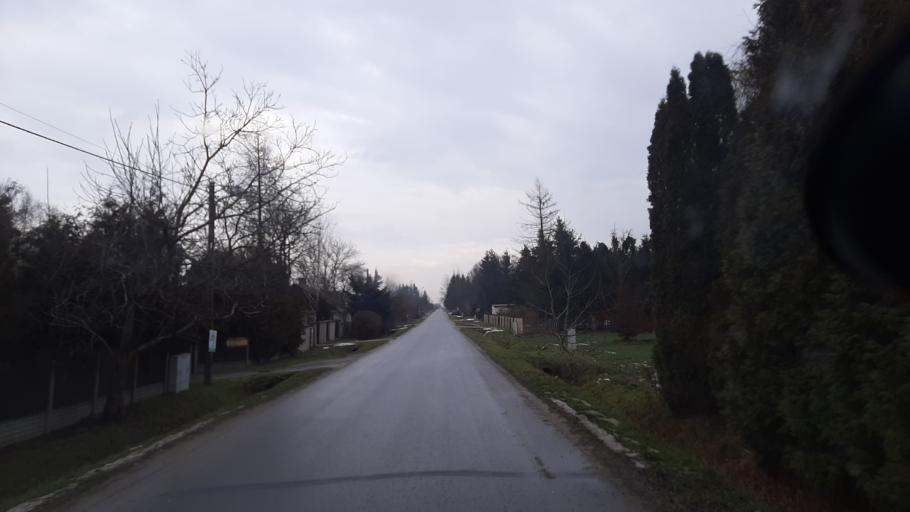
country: PL
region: Lublin Voivodeship
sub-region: Powiat lubelski
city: Jastkow
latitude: 51.3434
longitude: 22.4920
